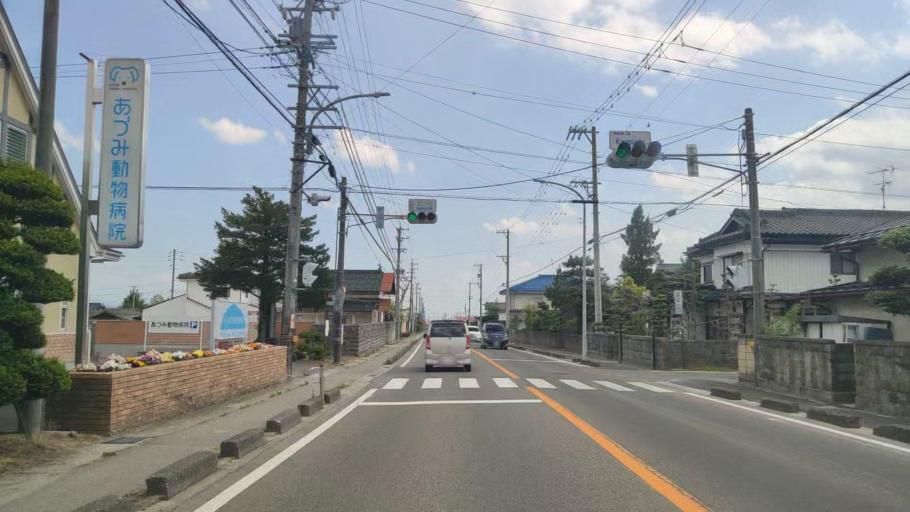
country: JP
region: Nagano
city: Omachi
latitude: 36.4718
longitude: 137.8484
